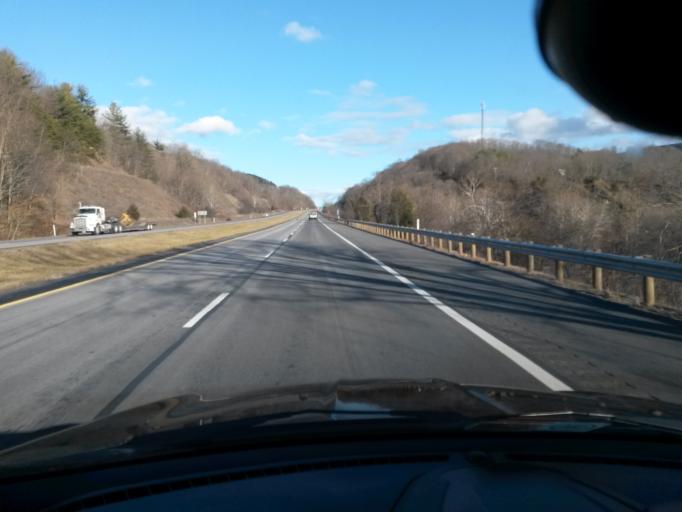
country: US
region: Virginia
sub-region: Giles County
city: Narrows
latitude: 37.3558
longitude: -80.8991
